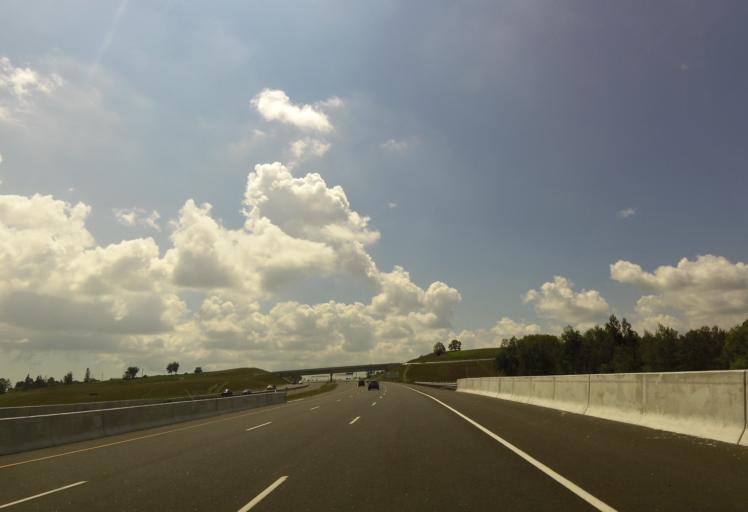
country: CA
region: Ontario
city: Pickering
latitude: 43.9310
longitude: -79.0852
